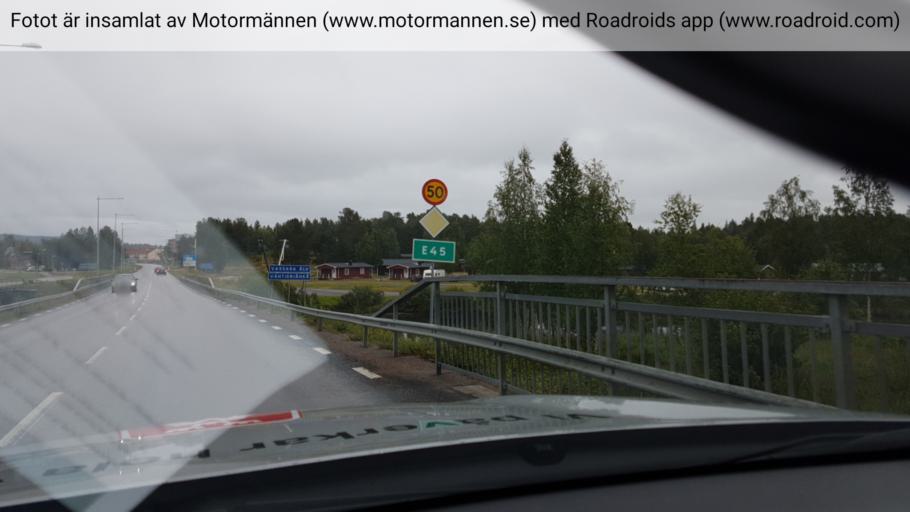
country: SE
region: Norrbotten
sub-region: Gallivare Kommun
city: Gaellivare
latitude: 67.1272
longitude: 20.6696
